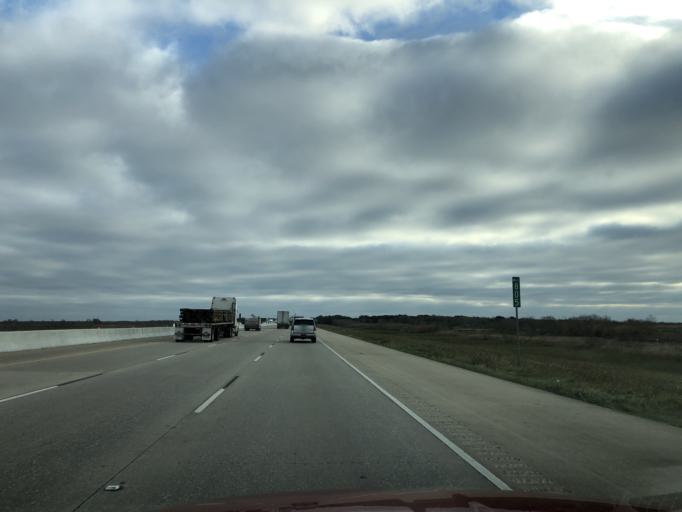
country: US
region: Texas
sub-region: Chambers County
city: Old River-Winfree
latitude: 29.8340
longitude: -94.7801
